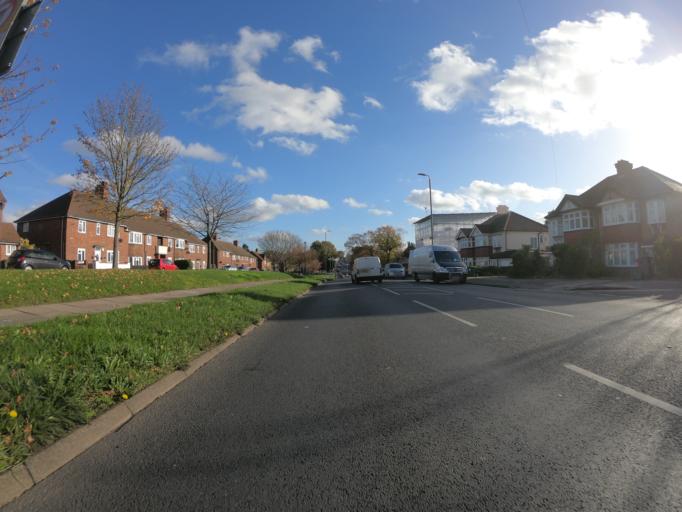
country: GB
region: England
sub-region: Greater London
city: Chislehurst
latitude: 51.4258
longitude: 0.0569
